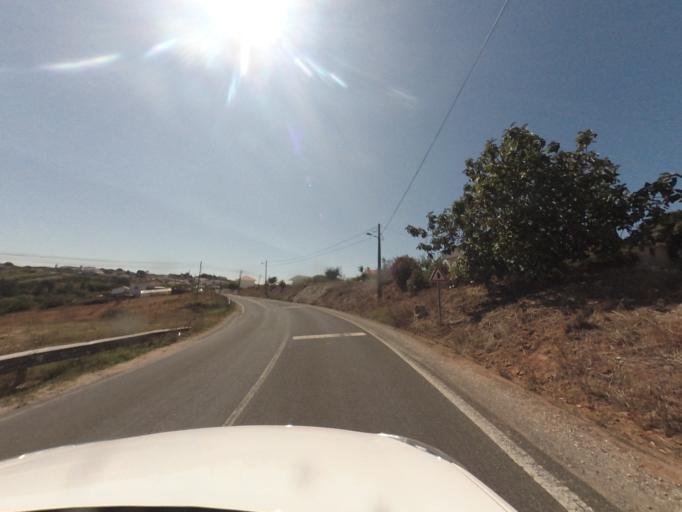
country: PT
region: Leiria
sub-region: Alcobaca
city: Turquel
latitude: 39.4863
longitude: -8.9829
